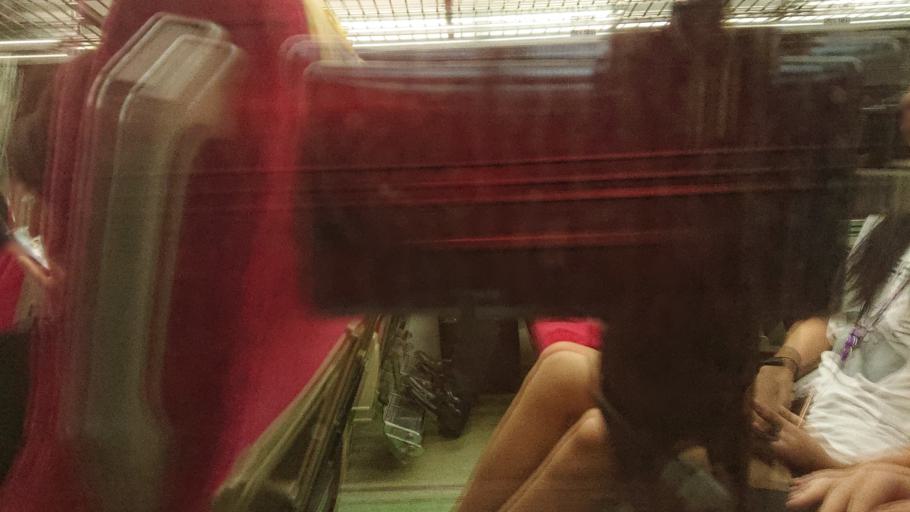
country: TW
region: Taiwan
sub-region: Yilan
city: Yilan
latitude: 24.9456
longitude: 121.9017
